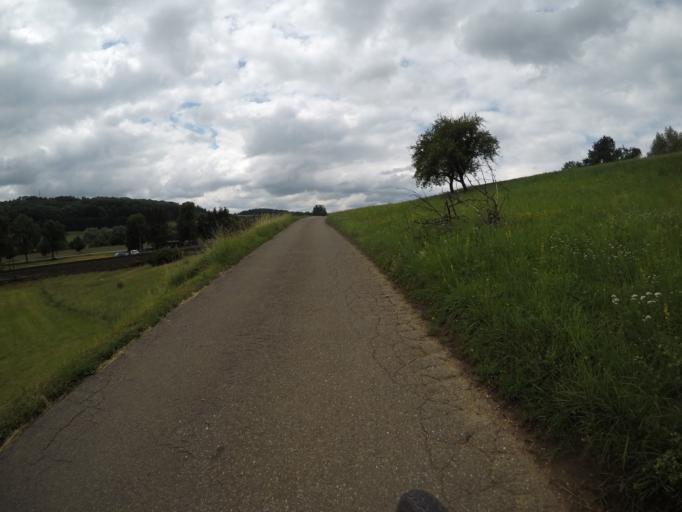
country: DE
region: Baden-Wuerttemberg
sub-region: Regierungsbezirk Stuttgart
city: Ebersbach an der Fils
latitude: 48.7145
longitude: 9.5027
